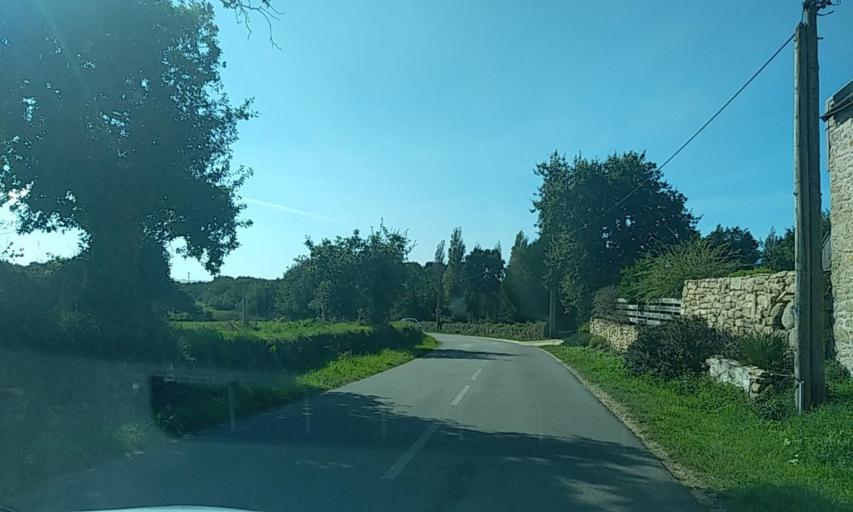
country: FR
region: Brittany
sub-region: Departement du Morbihan
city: Ploemeur
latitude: 47.7197
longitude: -3.4473
